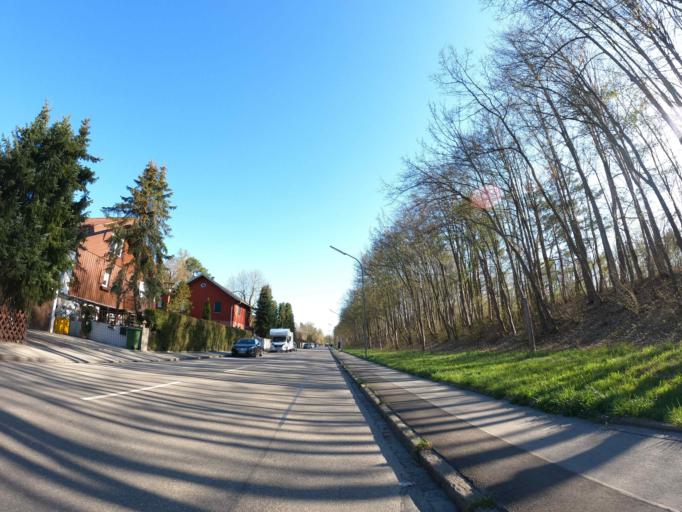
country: DE
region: Bavaria
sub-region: Upper Bavaria
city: Neubiberg
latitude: 48.0685
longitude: 11.6531
